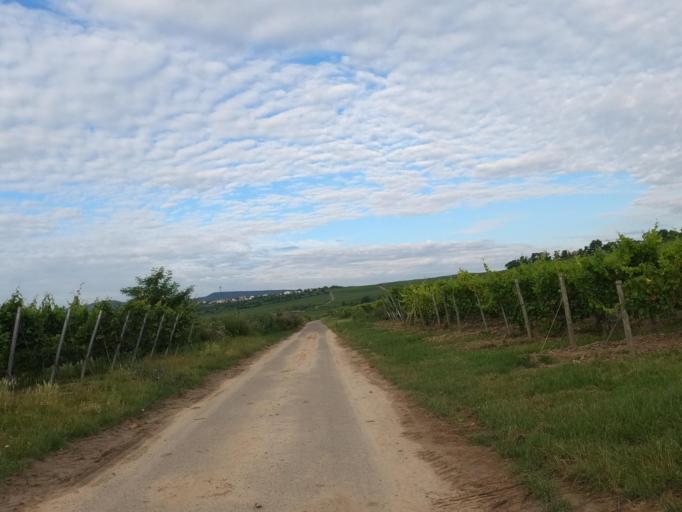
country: DE
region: Rheinland-Pfalz
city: Dackenheim
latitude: 49.5190
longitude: 8.1998
